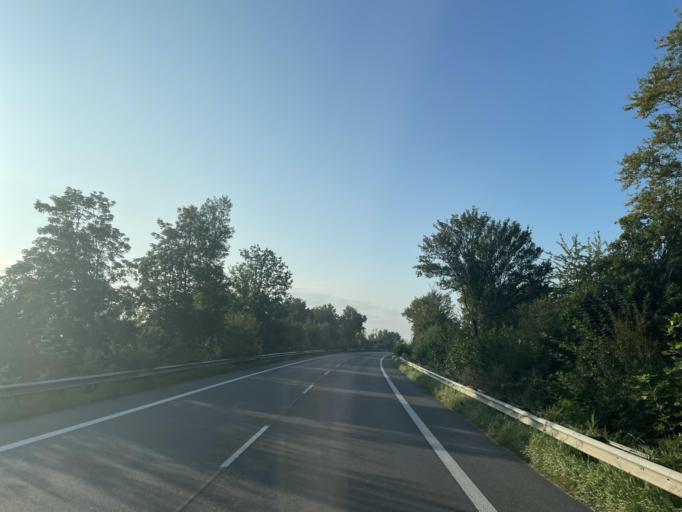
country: DE
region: North Rhine-Westphalia
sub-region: Regierungsbezirk Dusseldorf
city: Neubrueck
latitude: 51.1731
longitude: 6.5913
